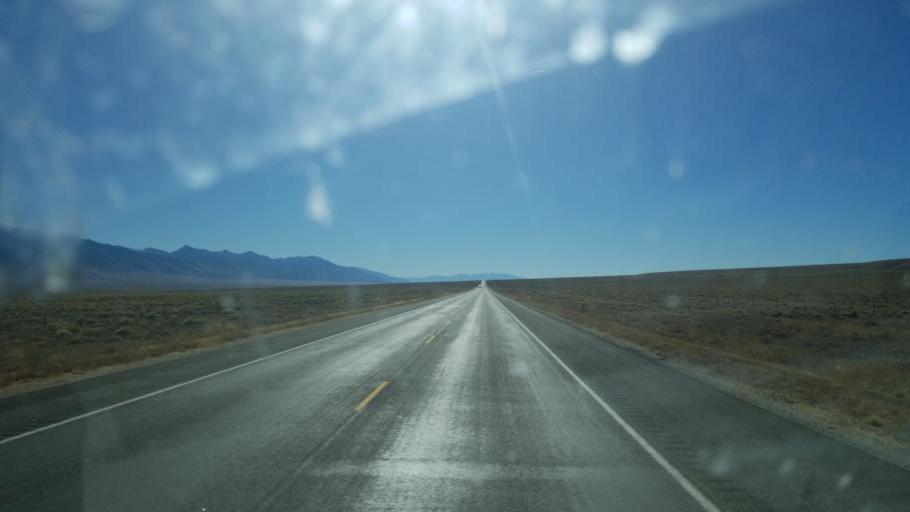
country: US
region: Colorado
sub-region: Chaffee County
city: Salida
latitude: 38.3124
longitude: -105.9976
